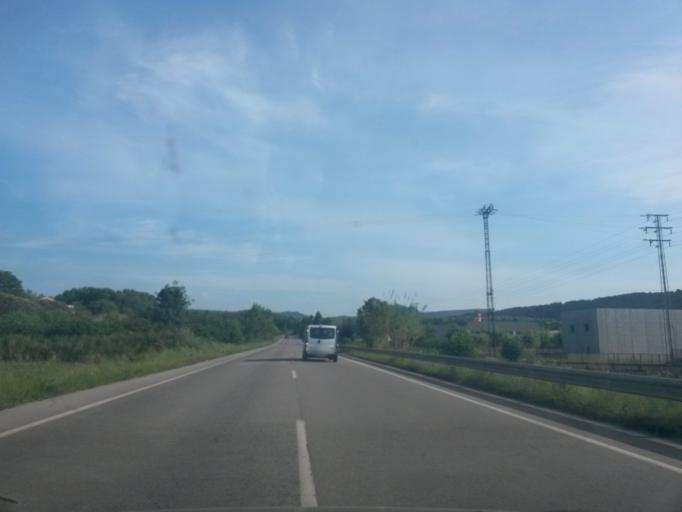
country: ES
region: Catalonia
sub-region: Provincia de Girona
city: la Cellera de Ter
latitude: 41.9710
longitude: 2.6243
